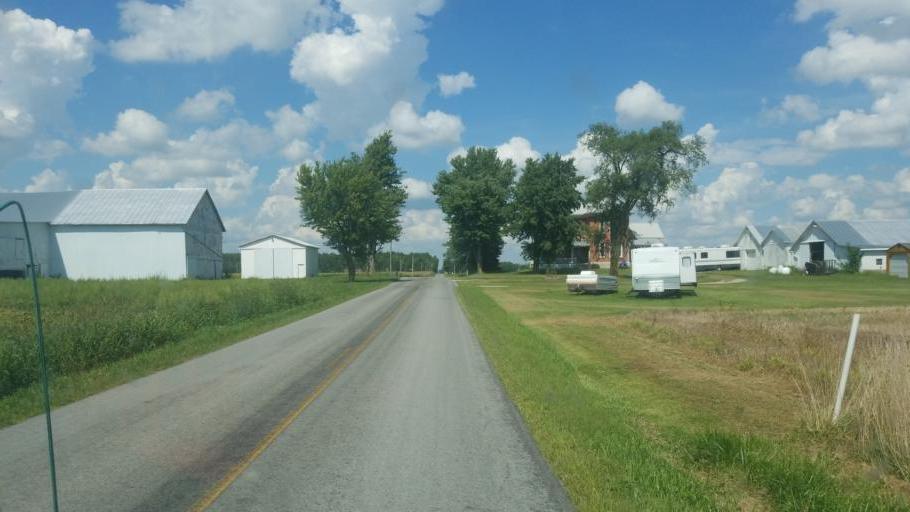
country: US
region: Ohio
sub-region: Wyandot County
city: Carey
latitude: 40.8652
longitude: -83.4191
